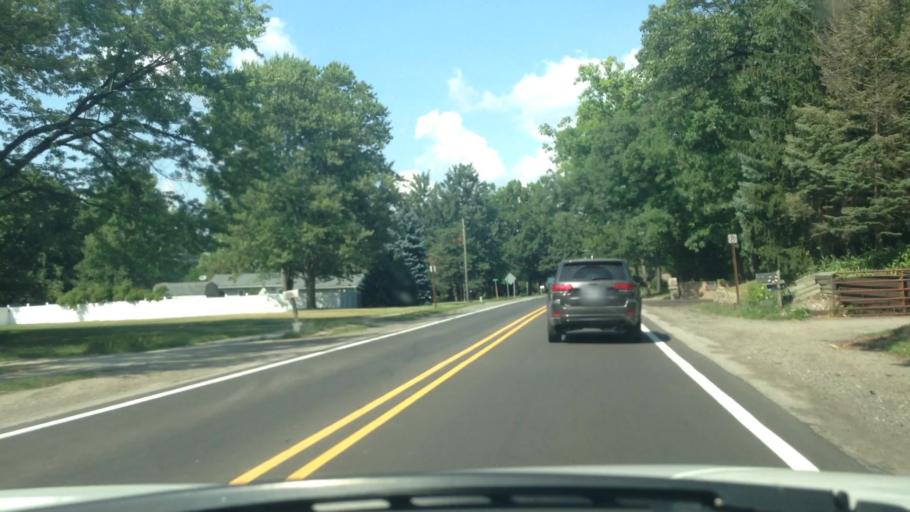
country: US
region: Michigan
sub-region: Oakland County
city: Waterford
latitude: 42.6957
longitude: -83.3724
